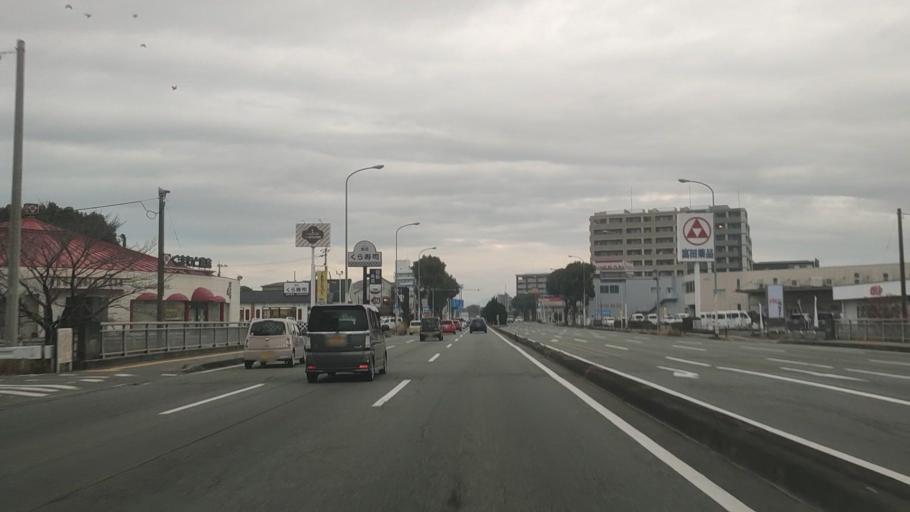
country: JP
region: Kumamoto
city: Kumamoto
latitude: 32.8112
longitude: 130.7493
